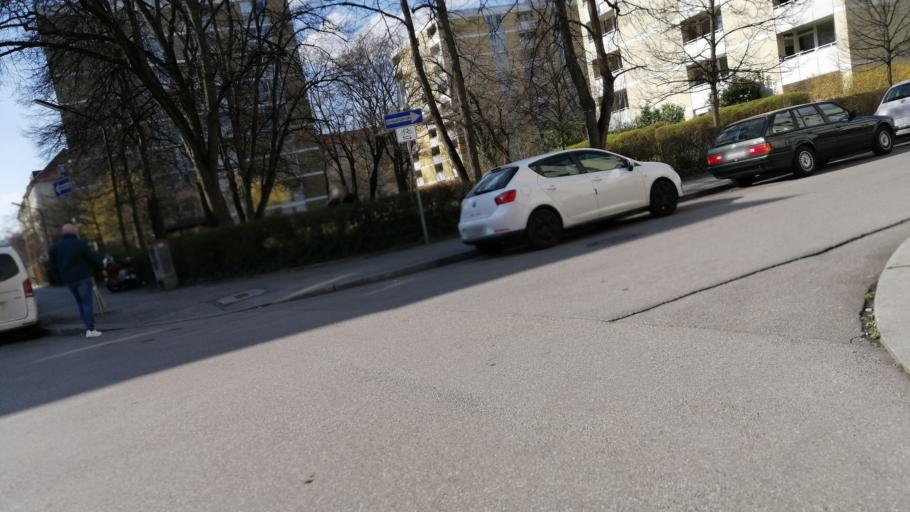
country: DE
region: Bavaria
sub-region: Upper Bavaria
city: Munich
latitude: 48.1657
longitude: 11.5773
